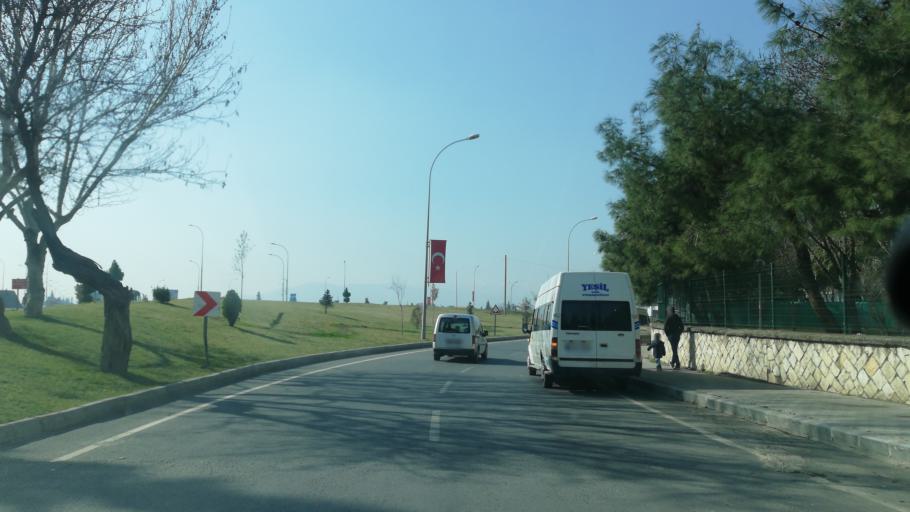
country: TR
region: Kahramanmaras
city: Kahramanmaras
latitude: 37.5697
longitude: 36.9247
